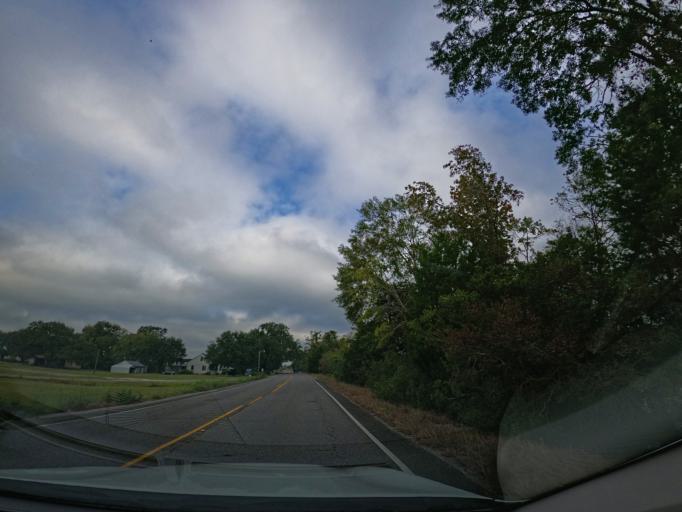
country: US
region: Louisiana
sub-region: Terrebonne Parish
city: Bayou Cane
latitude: 29.5791
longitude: -90.8133
